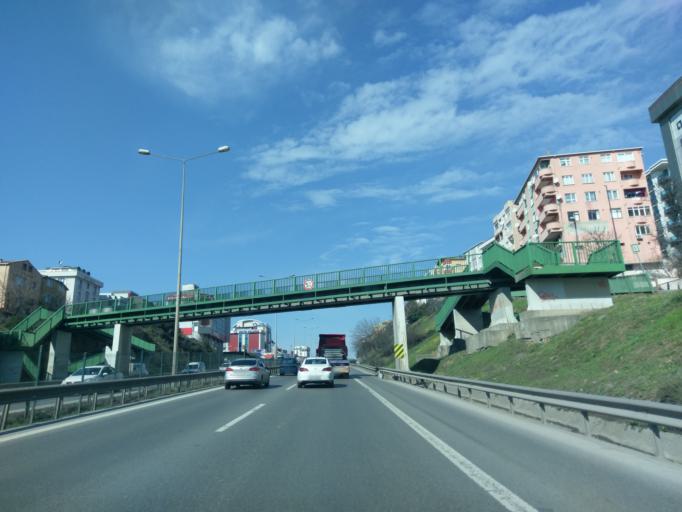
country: TR
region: Istanbul
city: Pendik
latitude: 40.8582
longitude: 29.2859
